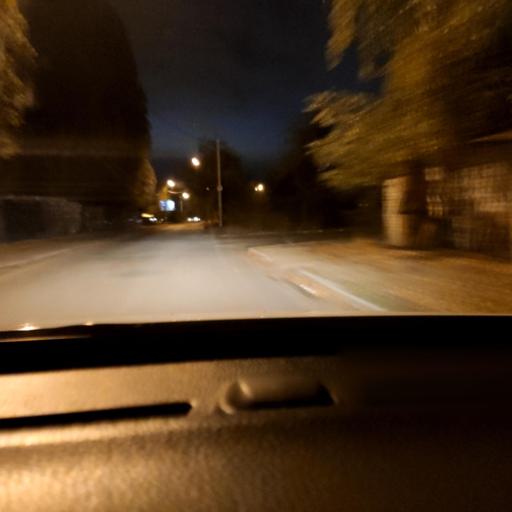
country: RU
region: Voronezj
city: Podgornoye
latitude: 51.7282
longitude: 39.1977
